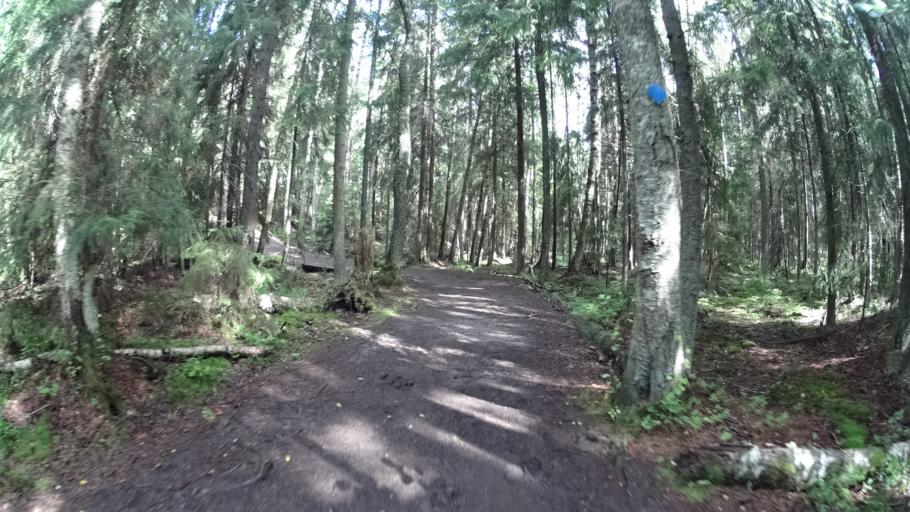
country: FI
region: Uusimaa
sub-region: Helsinki
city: Kauniainen
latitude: 60.3367
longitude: 24.6866
